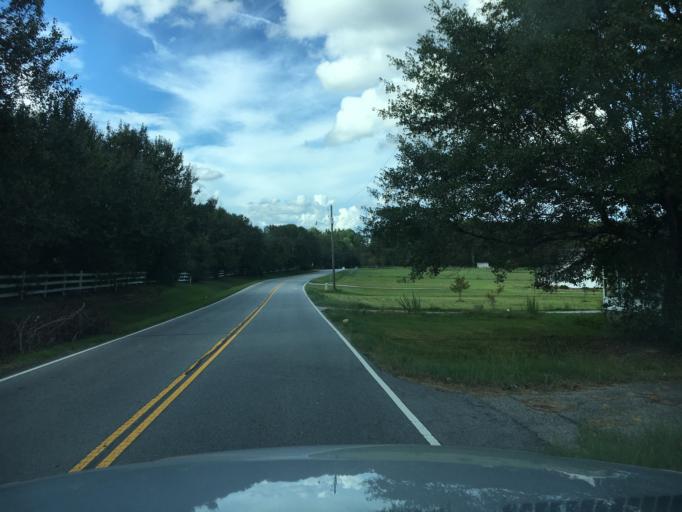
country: US
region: South Carolina
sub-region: Greenville County
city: Fountain Inn
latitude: 34.7051
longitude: -82.1794
